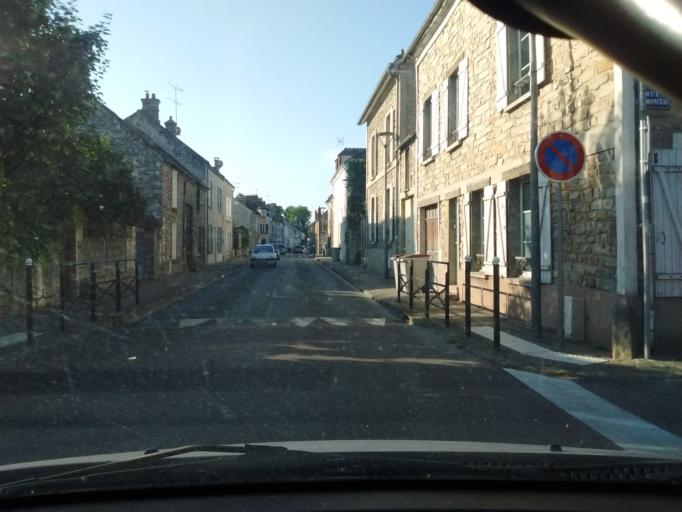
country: FR
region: Ile-de-France
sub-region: Departement de l'Essonne
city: Milly-la-Foret
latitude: 48.4060
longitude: 2.4689
